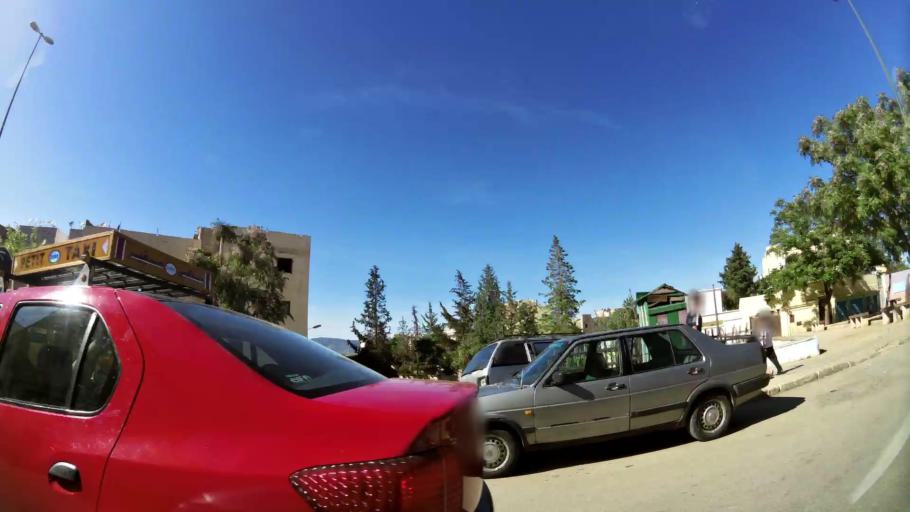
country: MA
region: Fes-Boulemane
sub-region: Fes
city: Fes
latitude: 34.0185
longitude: -4.9681
